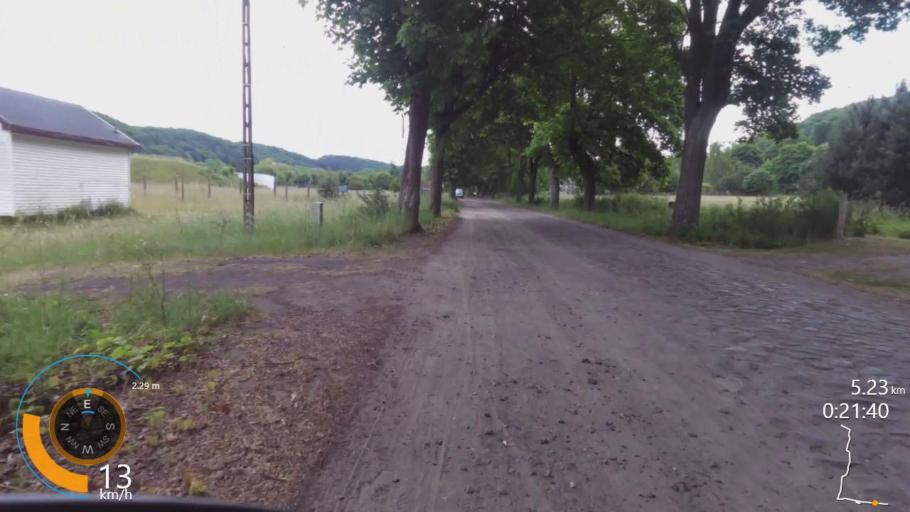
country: PL
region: West Pomeranian Voivodeship
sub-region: Powiat kamienski
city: Miedzyzdroje
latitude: 53.8787
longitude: 14.4480
